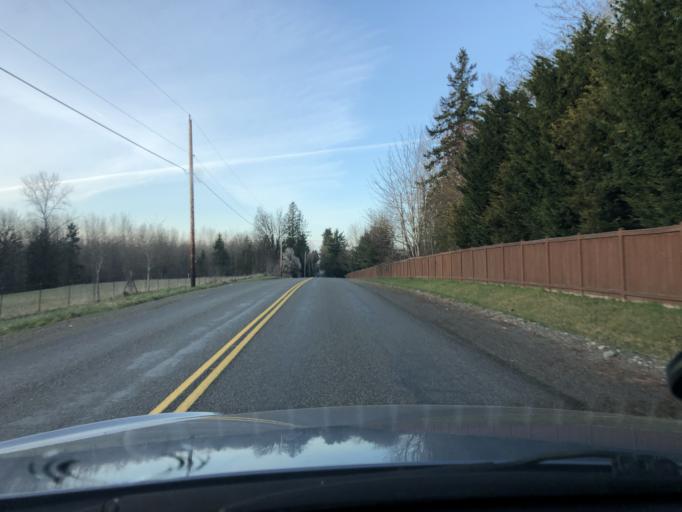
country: US
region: Washington
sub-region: Pierce County
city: Bonney Lake
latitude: 47.2049
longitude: -122.1227
